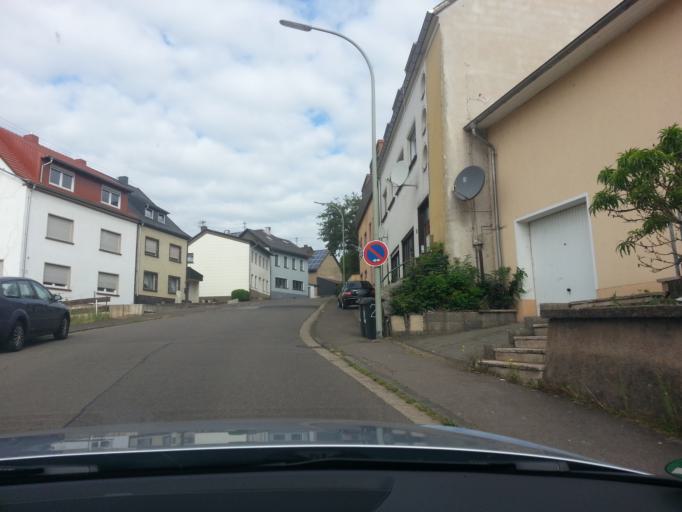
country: DE
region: Saarland
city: Schmelz
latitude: 49.4449
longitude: 6.8485
